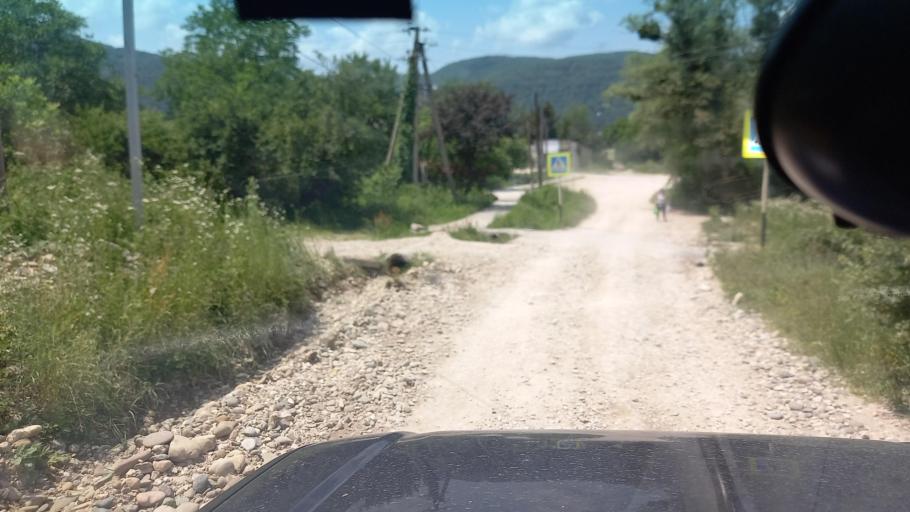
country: RU
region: Adygeya
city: Kamennomostskiy
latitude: 44.2910
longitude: 40.1852
